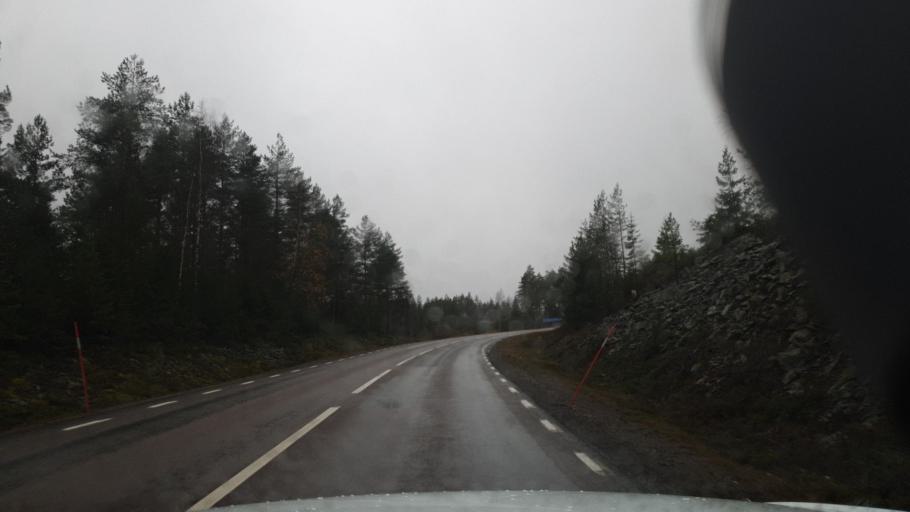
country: SE
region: Vaermland
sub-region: Sunne Kommun
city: Sunne
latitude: 59.6989
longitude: 13.1045
